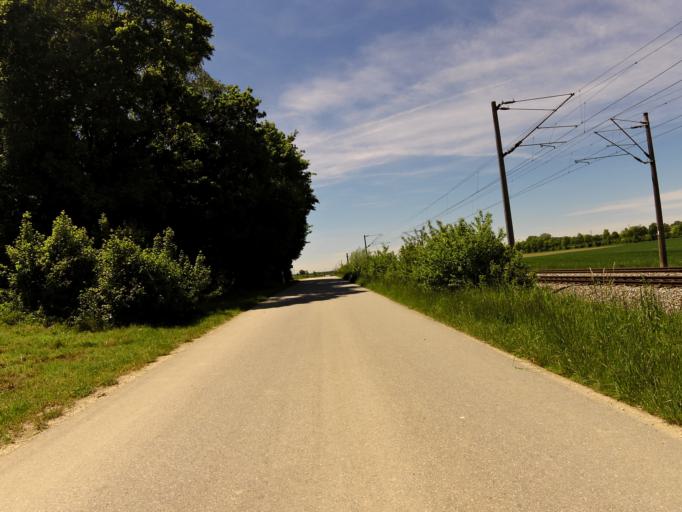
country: DE
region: Bavaria
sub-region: Upper Bavaria
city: Langenbach
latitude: 48.4289
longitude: 11.8380
